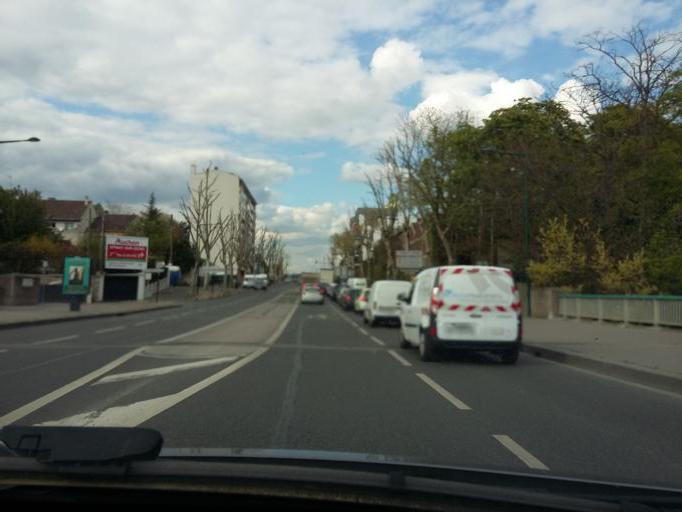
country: FR
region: Ile-de-France
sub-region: Departement de Seine-Saint-Denis
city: Epinay-sur-Seine
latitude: 48.9516
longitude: 2.3072
